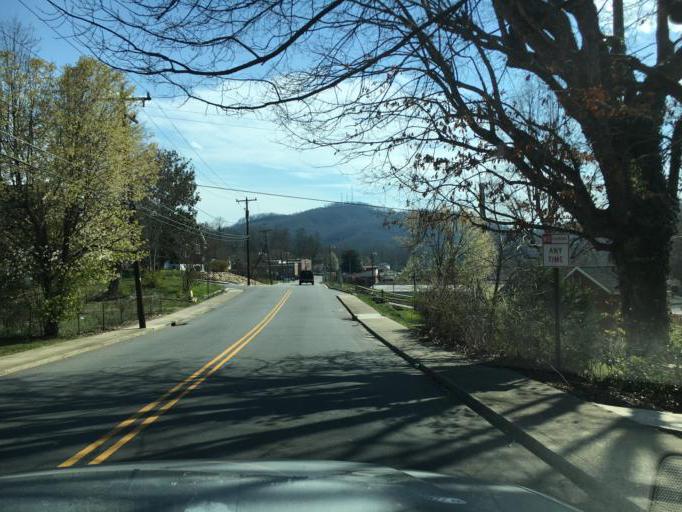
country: US
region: North Carolina
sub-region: McDowell County
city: Marion
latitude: 35.6821
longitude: -81.9919
